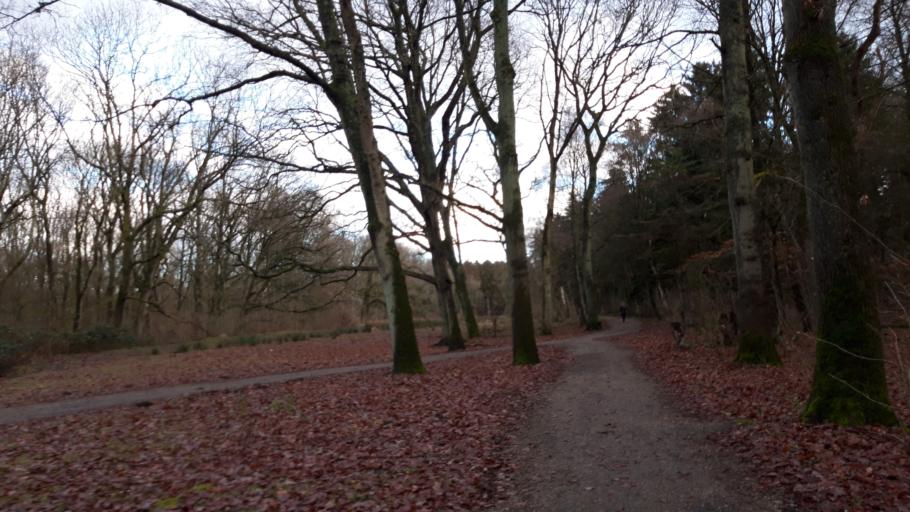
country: NL
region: South Holland
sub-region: Gemeente Rotterdam
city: Rotterdam
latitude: 51.9437
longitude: 4.5158
